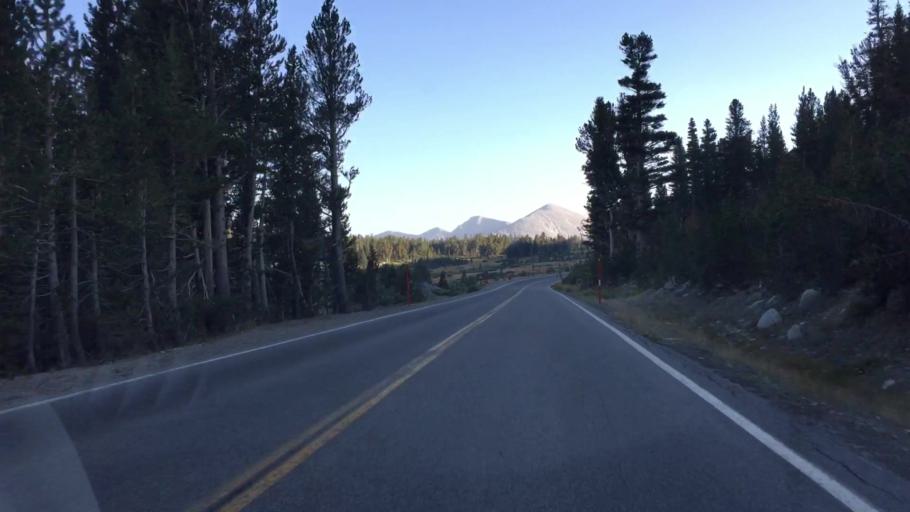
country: US
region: California
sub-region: Mono County
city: Bridgeport
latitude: 37.9205
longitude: -119.2550
